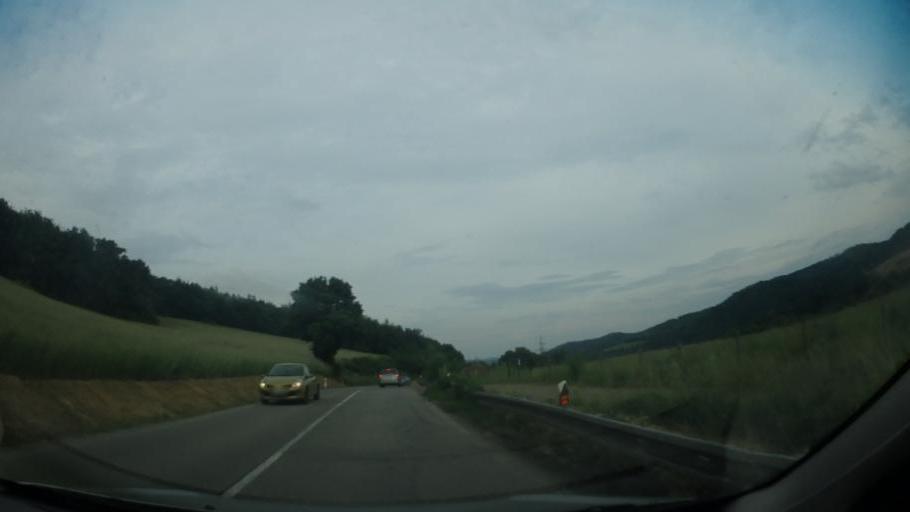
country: CZ
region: South Moravian
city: Predklasteri
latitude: 49.3631
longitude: 16.3833
